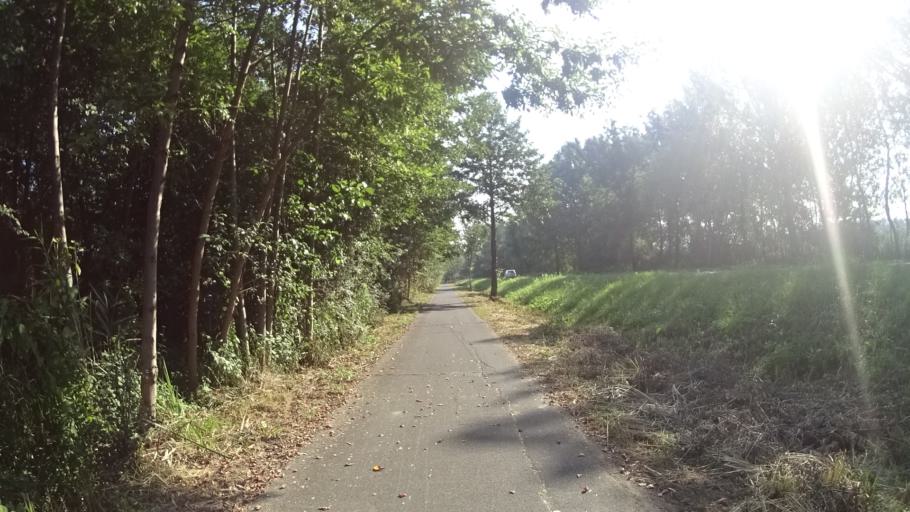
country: HU
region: Somogy
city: Balatonbereny
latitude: 46.7017
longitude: 17.2792
